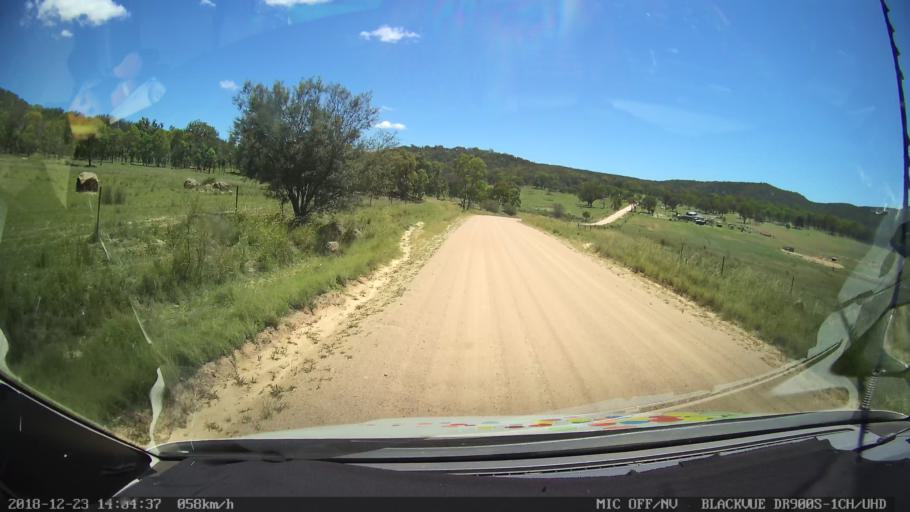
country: AU
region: New South Wales
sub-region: Tamworth Municipality
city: Manilla
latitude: -30.6228
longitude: 151.0886
